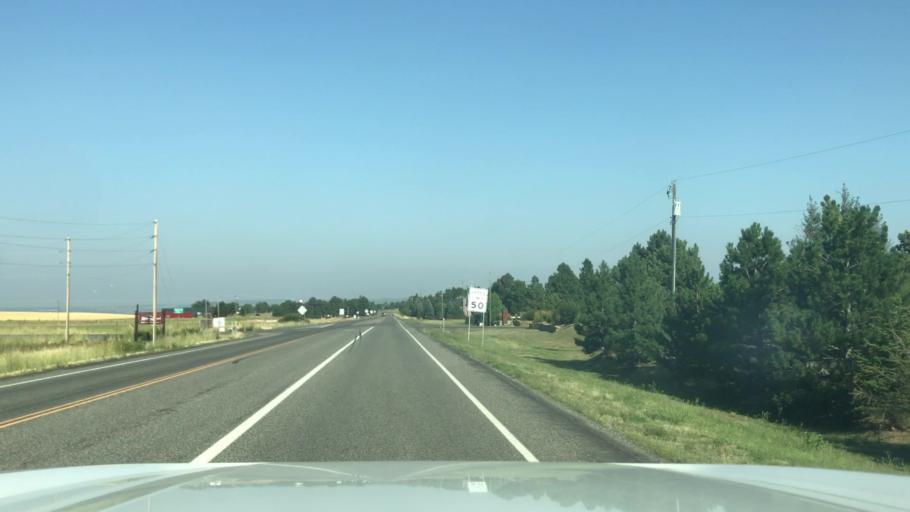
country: US
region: Montana
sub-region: Yellowstone County
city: Billings
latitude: 45.8055
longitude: -108.5920
